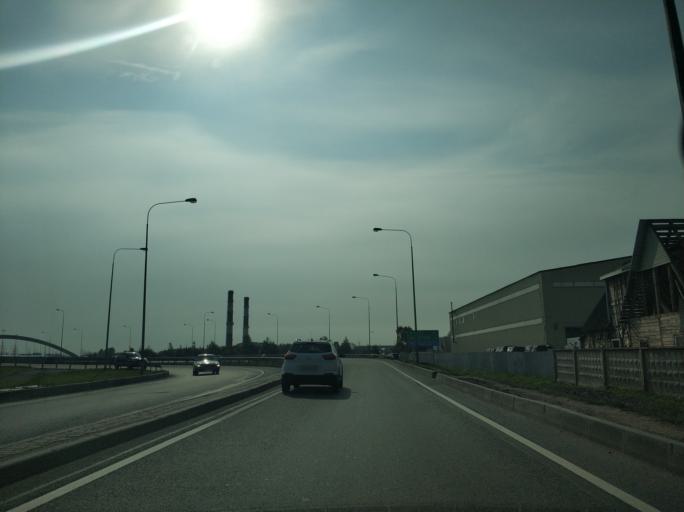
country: RU
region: Leningrad
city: Murino
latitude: 60.0354
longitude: 30.4391
